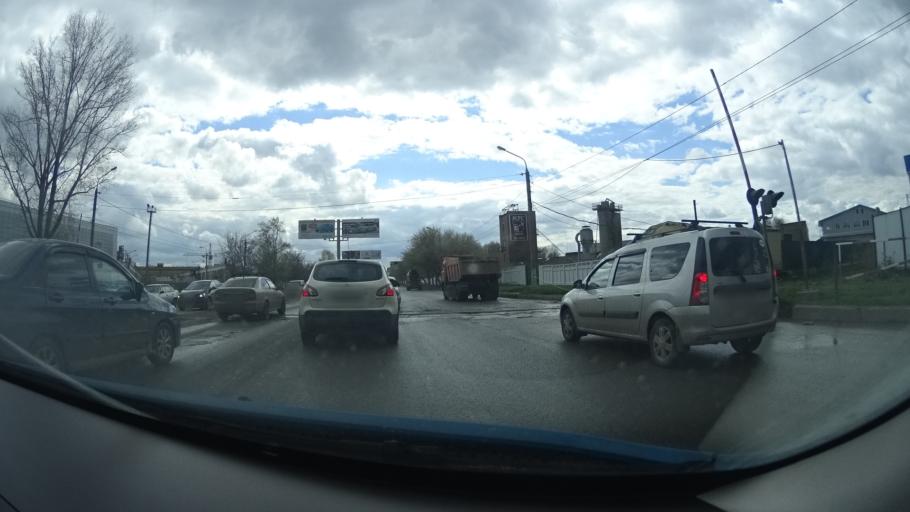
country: RU
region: Bashkortostan
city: Ufa
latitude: 54.8037
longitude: 56.0815
